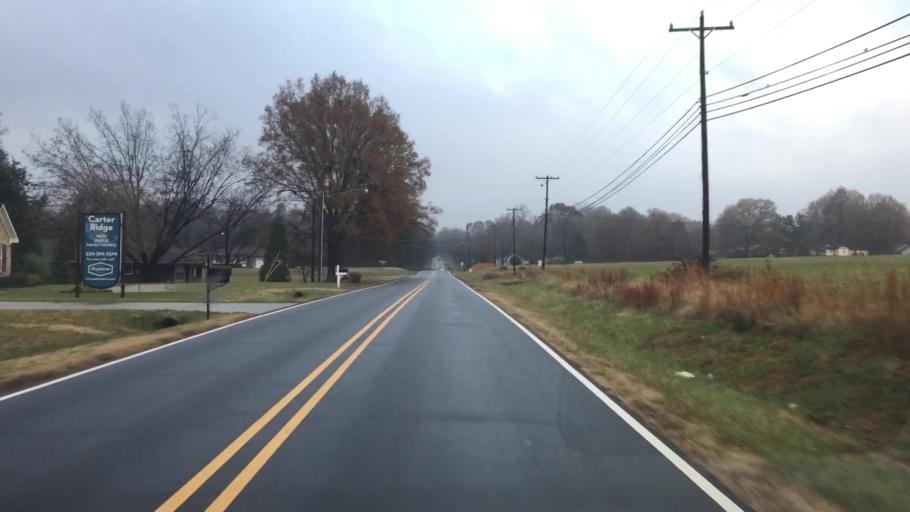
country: US
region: North Carolina
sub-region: Rockingham County
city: Reidsville
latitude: 36.3457
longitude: -79.6994
